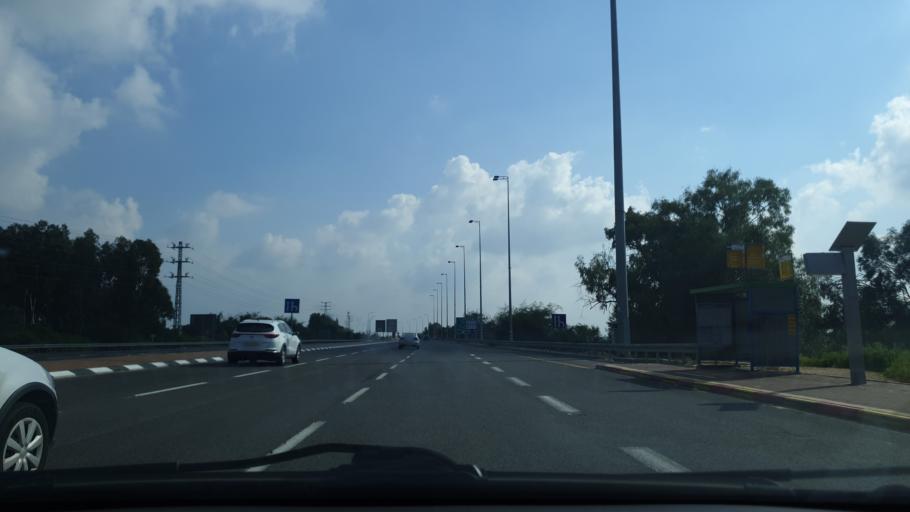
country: IL
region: Central District
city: Ramla
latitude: 31.9509
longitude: 34.8568
